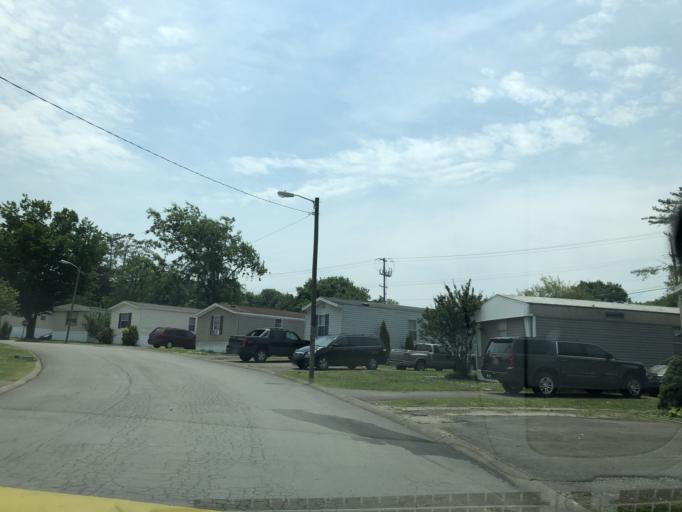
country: US
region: Tennessee
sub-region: Davidson County
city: Oak Hill
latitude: 36.0694
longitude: -86.6770
